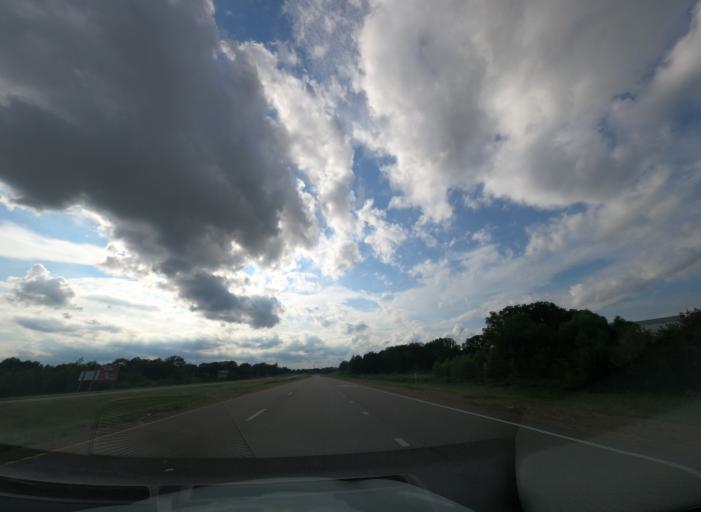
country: US
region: Tennessee
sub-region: Fayette County
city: Piperton
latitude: 34.9877
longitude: -89.6029
